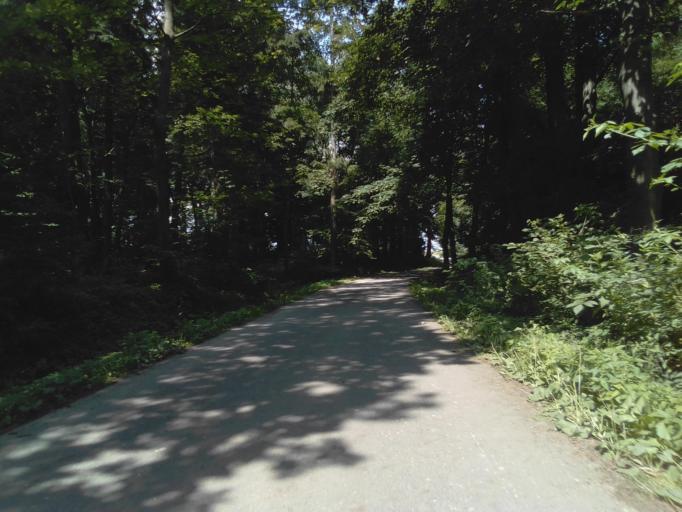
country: PL
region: Subcarpathian Voivodeship
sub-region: Powiat strzyzowski
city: Frysztak
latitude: 49.7918
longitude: 21.6011
